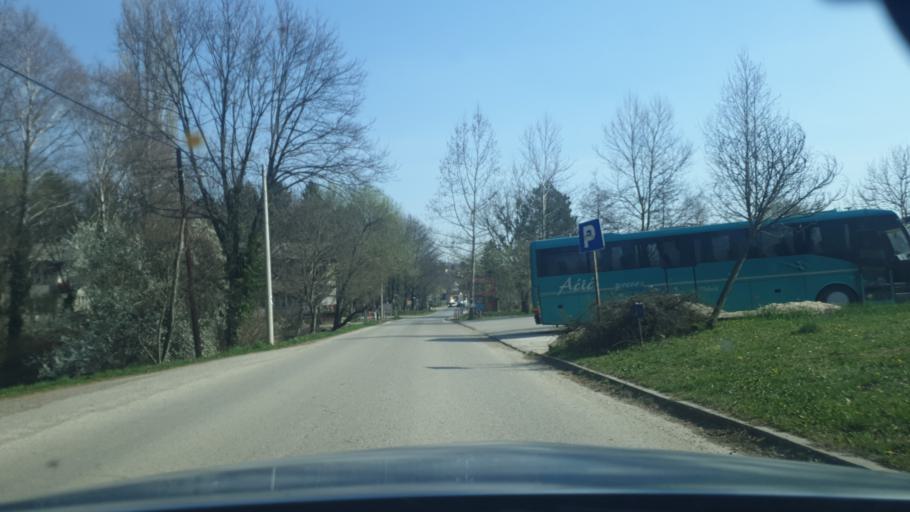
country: RS
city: Vrdnik
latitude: 45.1293
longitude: 19.7854
